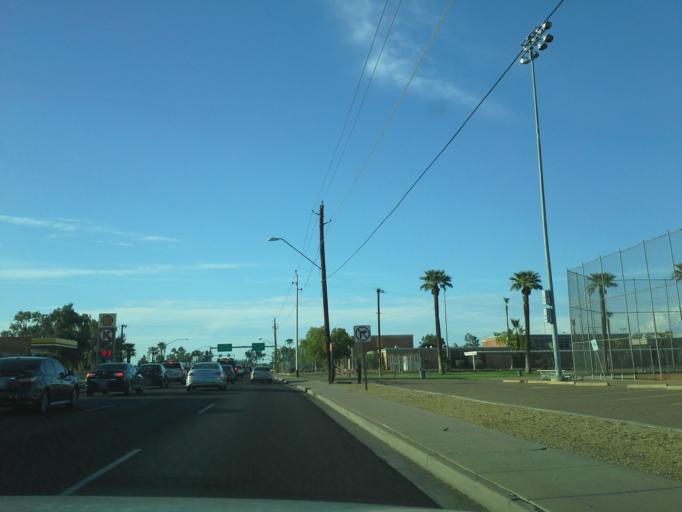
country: US
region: Arizona
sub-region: Maricopa County
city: Phoenix
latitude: 33.4564
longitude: -112.1344
